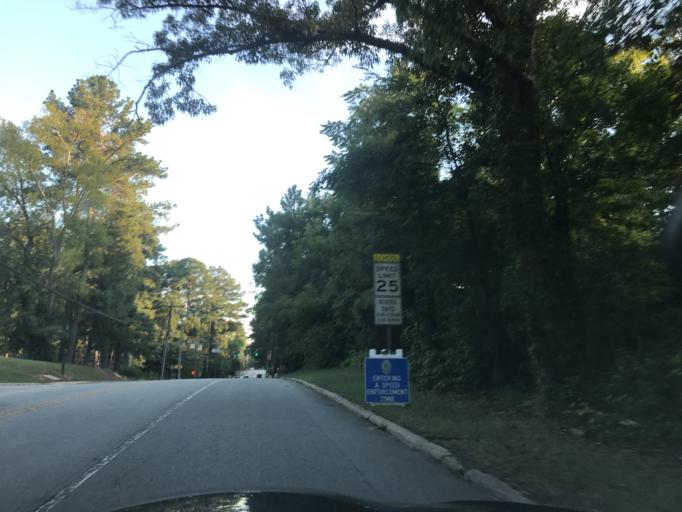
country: US
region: North Carolina
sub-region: Wake County
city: Raleigh
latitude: 35.7970
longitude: -78.6242
